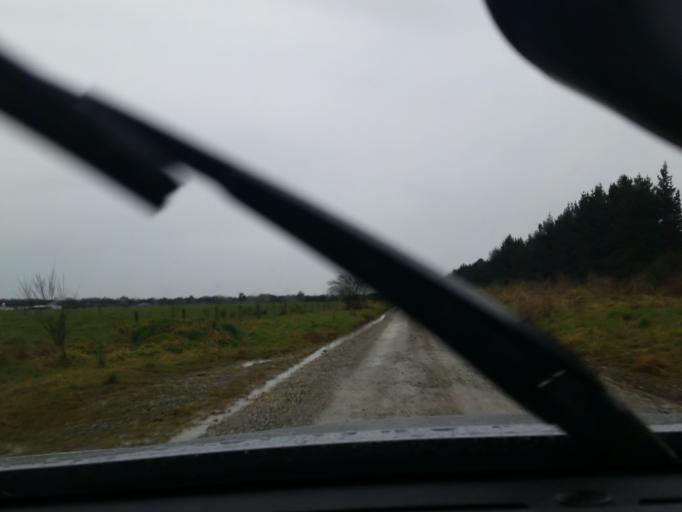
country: NZ
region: Southland
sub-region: Southland District
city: Winton
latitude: -46.2319
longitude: 168.4854
